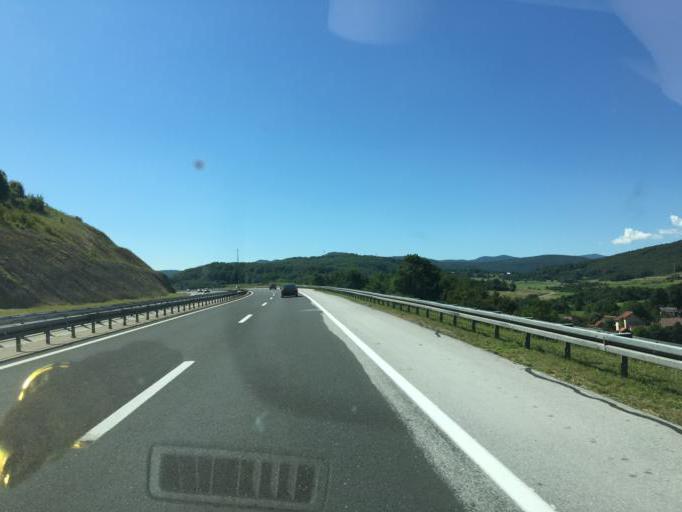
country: HR
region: Licko-Senjska
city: Otocac
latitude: 44.8991
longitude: 15.1839
